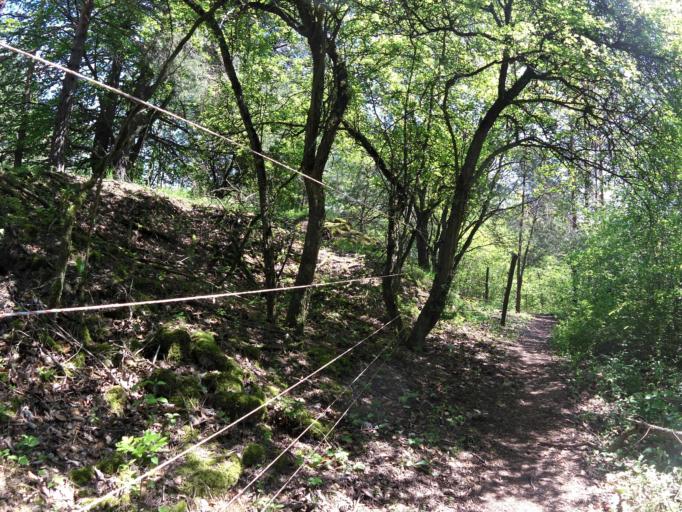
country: DE
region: Bavaria
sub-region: Regierungsbezirk Unterfranken
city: Theilheim
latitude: 49.7374
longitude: 10.0173
